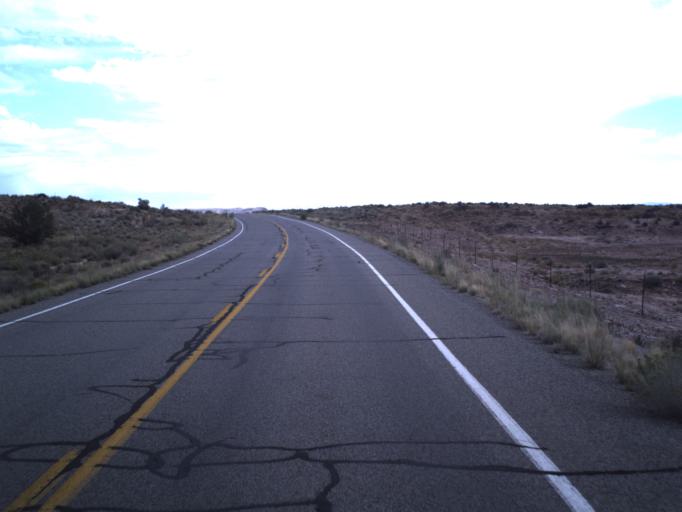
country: US
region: Utah
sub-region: San Juan County
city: Blanding
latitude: 37.2962
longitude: -109.4266
